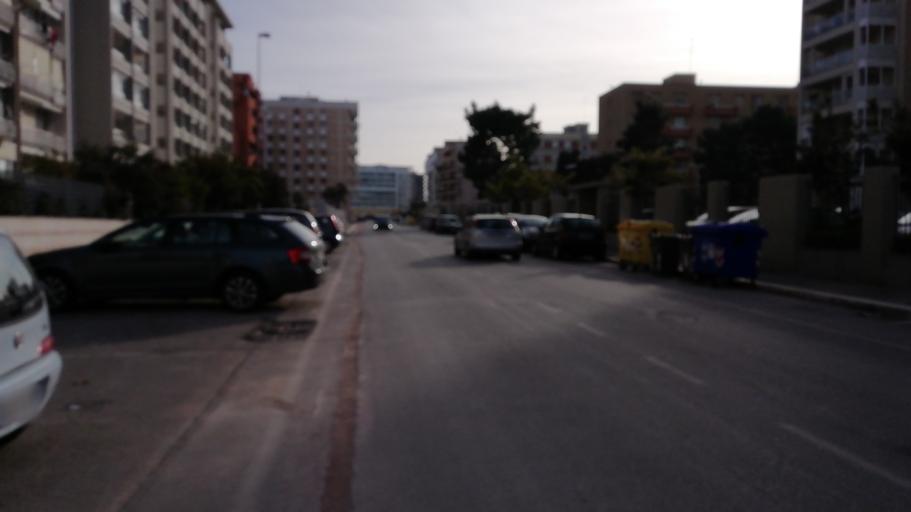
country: IT
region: Apulia
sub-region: Provincia di Bari
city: Triggiano
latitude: 41.1056
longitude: 16.9159
